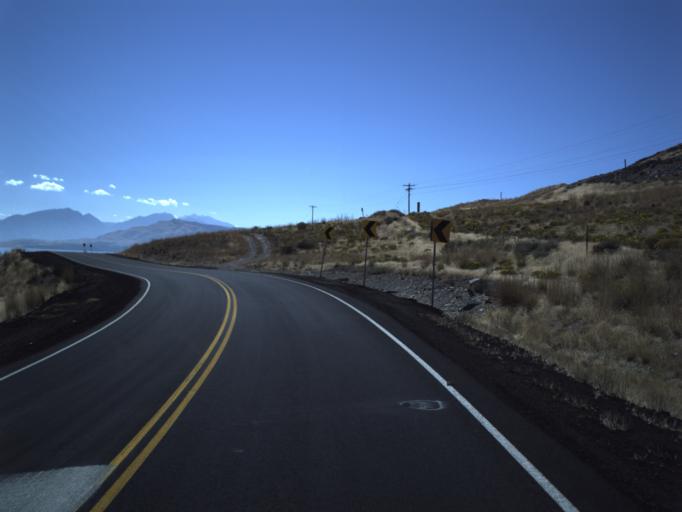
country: US
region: Utah
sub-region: Utah County
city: Saratoga Springs
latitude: 40.2535
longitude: -111.8671
